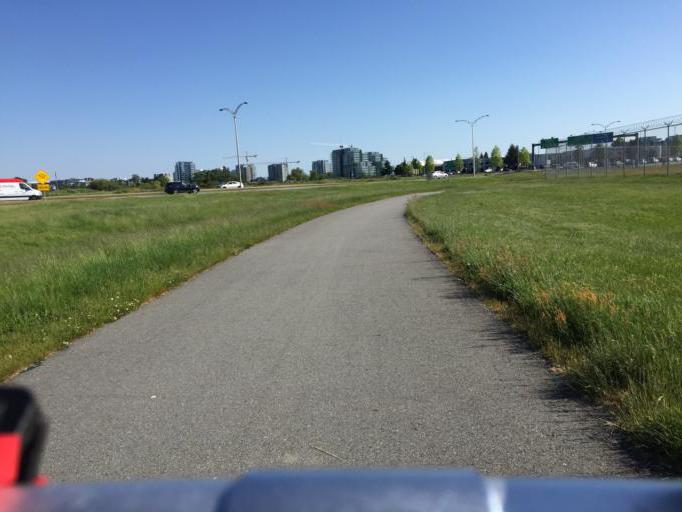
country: CA
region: British Columbia
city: Richmond
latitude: 49.1833
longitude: -123.1501
